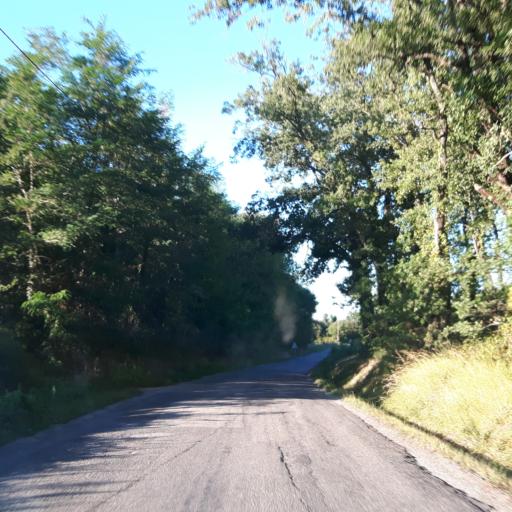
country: FR
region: Midi-Pyrenees
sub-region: Departement de la Haute-Garonne
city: Fronton
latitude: 43.8130
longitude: 1.3825
